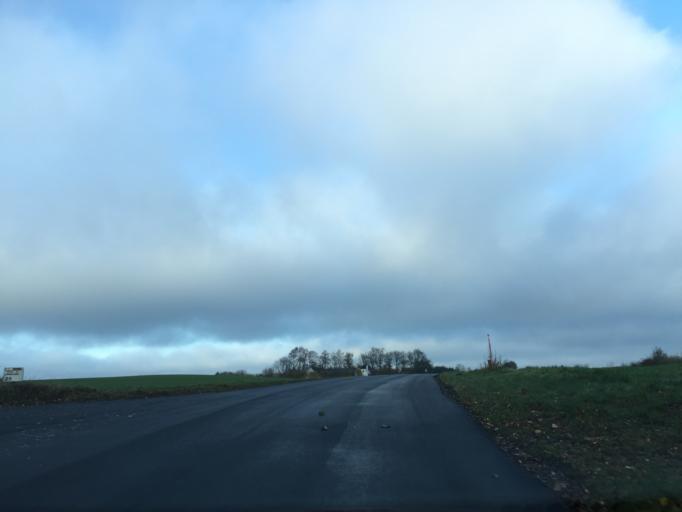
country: DK
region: Central Jutland
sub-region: Silkeborg Kommune
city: Svejbaek
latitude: 56.1615
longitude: 9.6918
